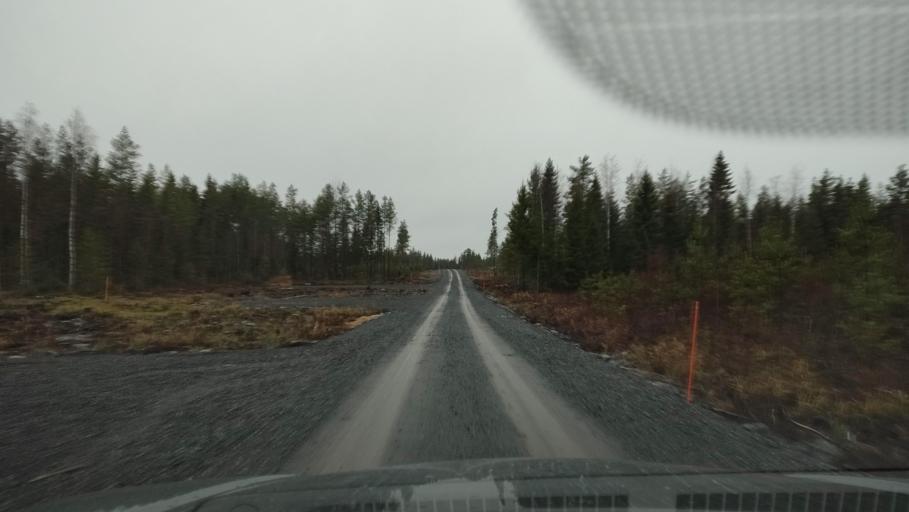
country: FI
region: Southern Ostrobothnia
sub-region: Suupohja
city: Karijoki
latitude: 62.1587
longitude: 21.5989
